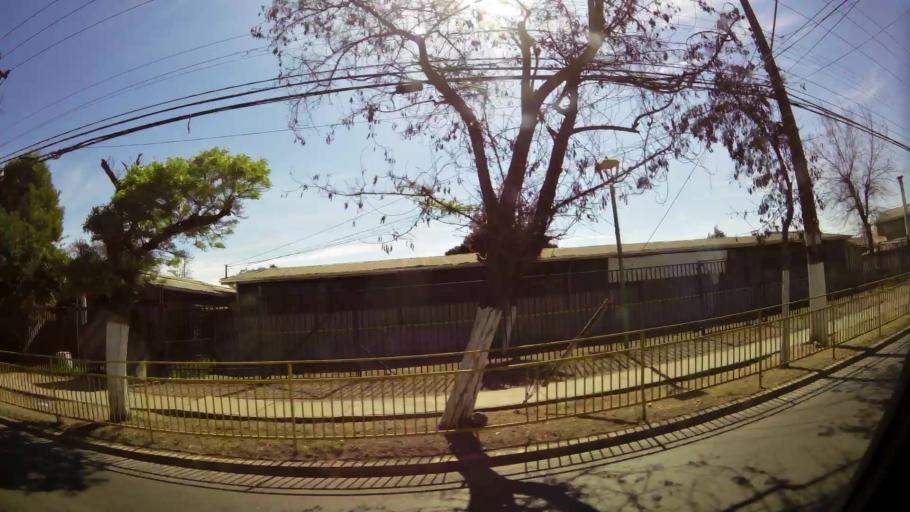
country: CL
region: Santiago Metropolitan
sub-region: Provincia de Santiago
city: Lo Prado
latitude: -33.4989
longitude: -70.7236
